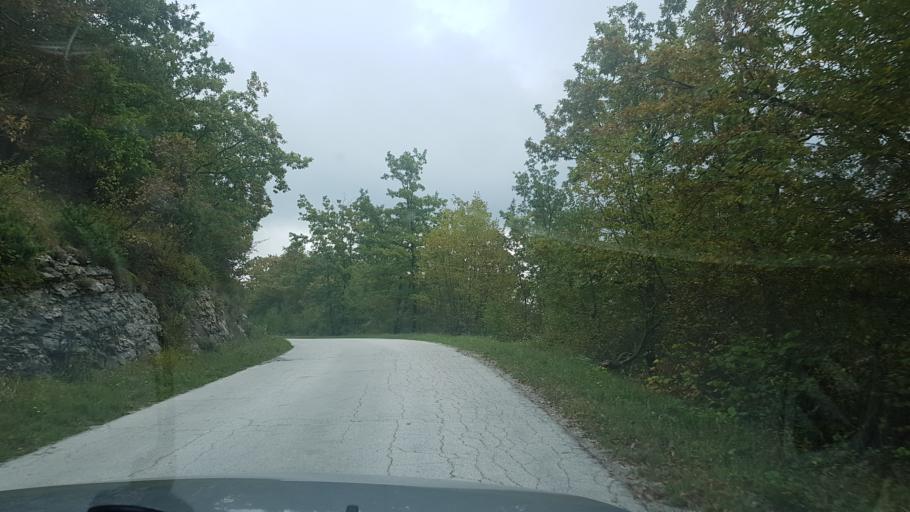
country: HR
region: Istarska
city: Buzet
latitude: 45.5057
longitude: 13.9780
